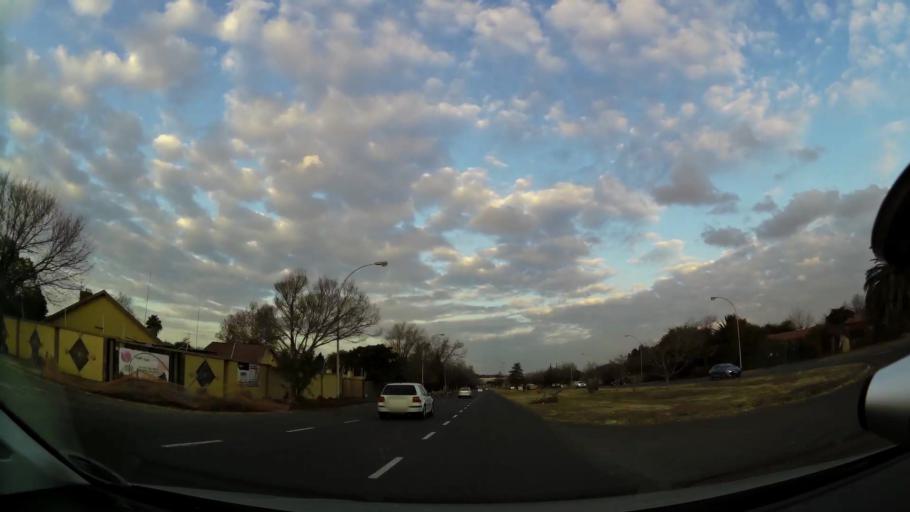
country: ZA
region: Orange Free State
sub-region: Mangaung Metropolitan Municipality
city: Bloemfontein
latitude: -29.1529
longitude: 26.1812
